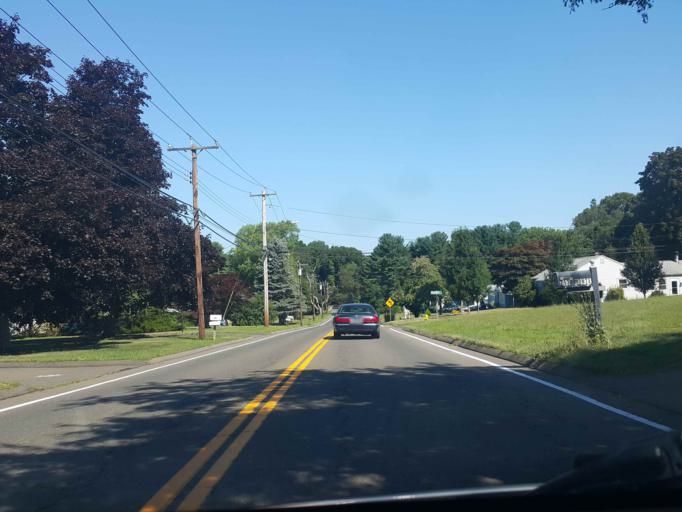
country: US
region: Connecticut
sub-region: New Haven County
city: North Branford
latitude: 41.3231
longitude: -72.7614
